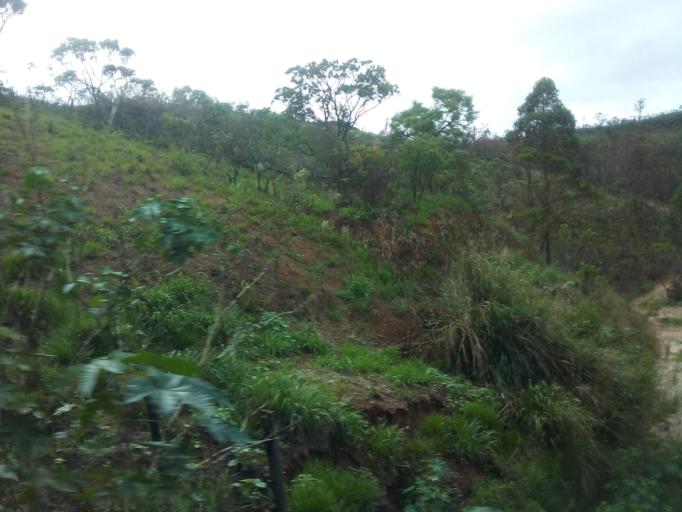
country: BR
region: Minas Gerais
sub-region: Caete
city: Caete
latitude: -19.9117
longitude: -43.6994
